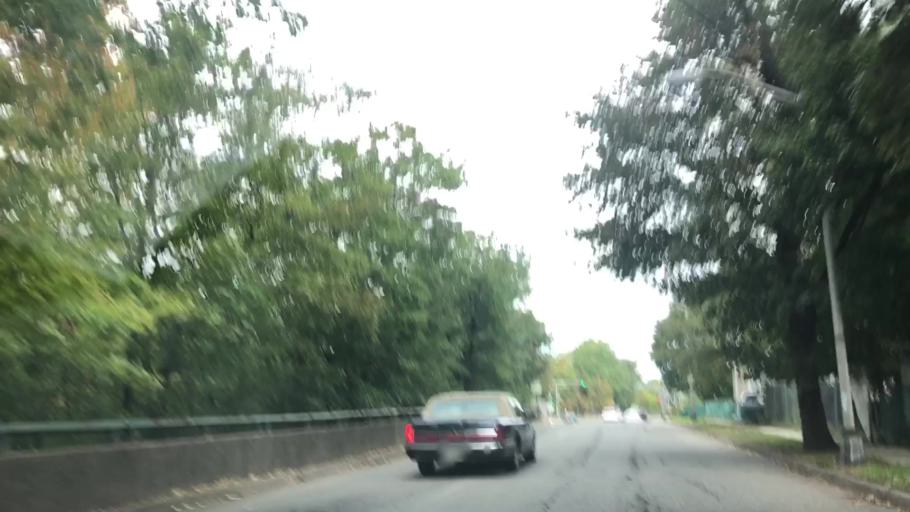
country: US
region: New Jersey
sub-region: Essex County
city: East Orange
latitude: 40.7707
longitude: -74.2041
